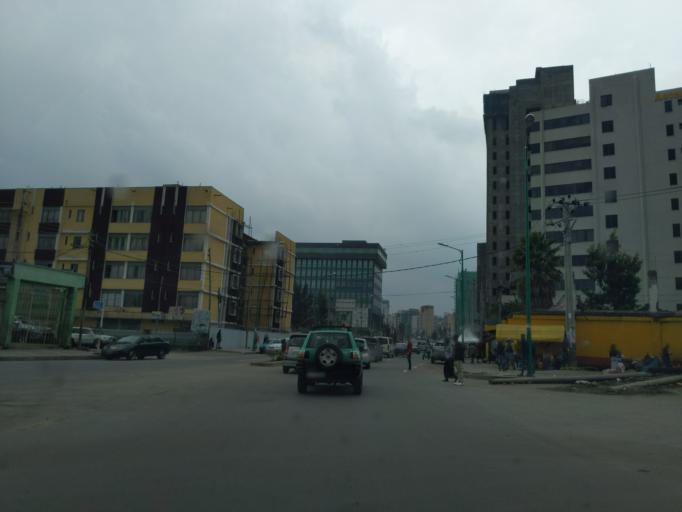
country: ET
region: Adis Abeba
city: Addis Ababa
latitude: 8.9881
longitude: 38.7652
